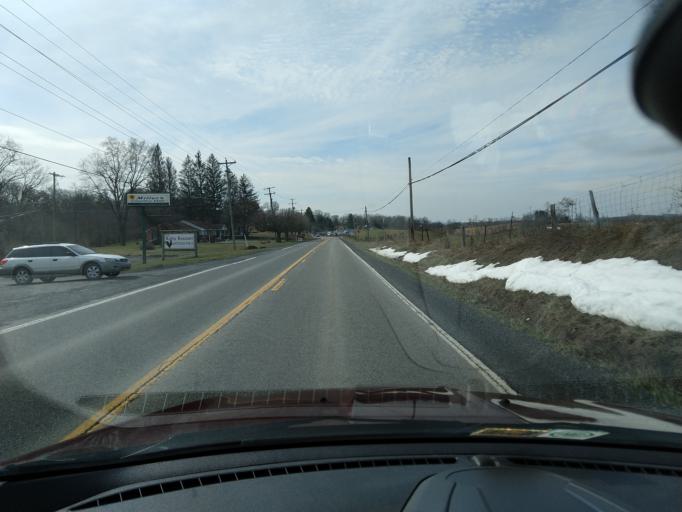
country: US
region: West Virginia
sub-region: Greenbrier County
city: Lewisburg
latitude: 37.8603
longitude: -80.4110
